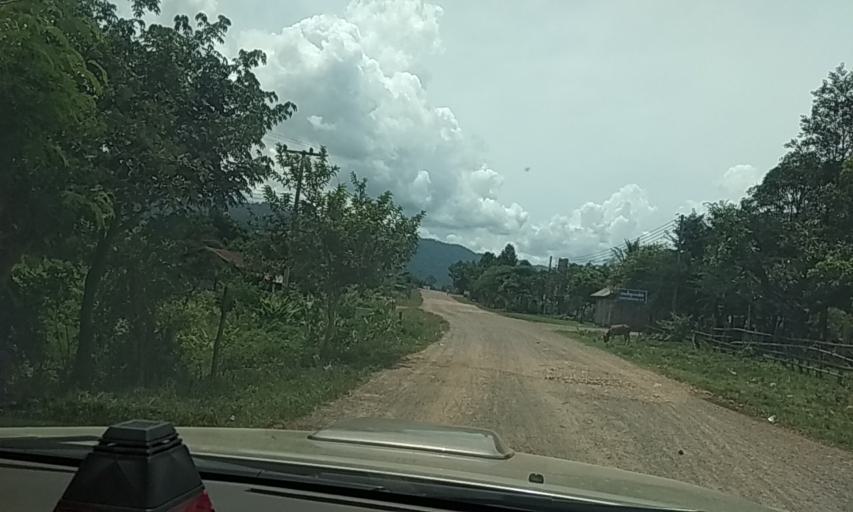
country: LA
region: Bolikhamxai
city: Ban Nahin
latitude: 18.1405
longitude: 104.7584
